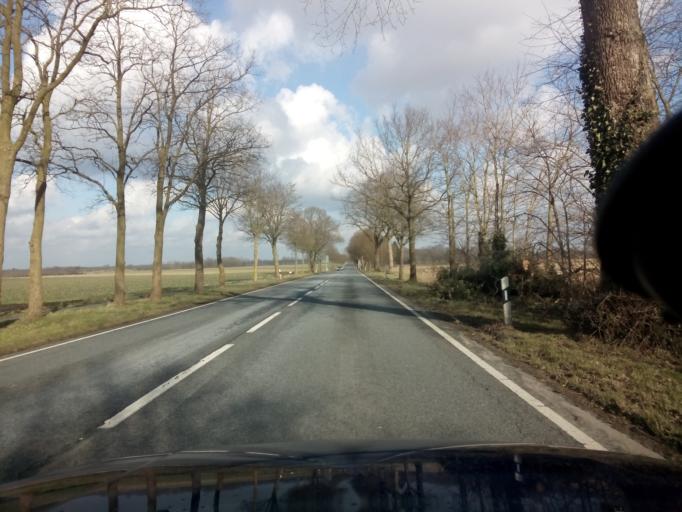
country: DE
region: Lower Saxony
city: Vollersode
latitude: 53.3259
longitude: 8.8934
